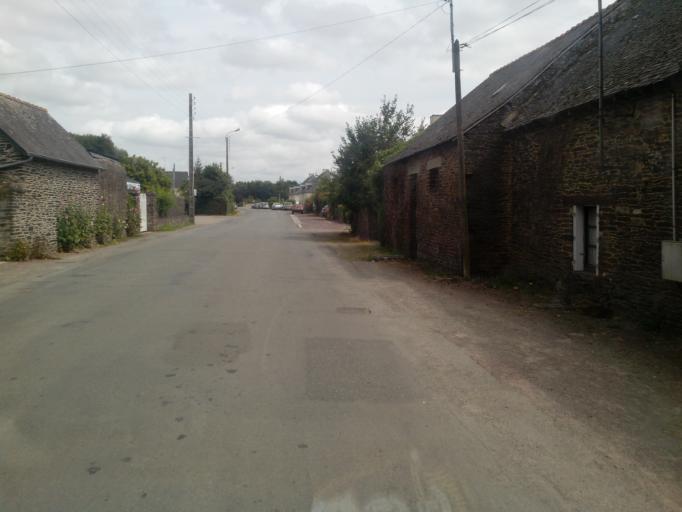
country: FR
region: Brittany
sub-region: Departement d'Ille-et-Vilaine
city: Plelan-le-Grand
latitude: 48.0013
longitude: -2.0959
